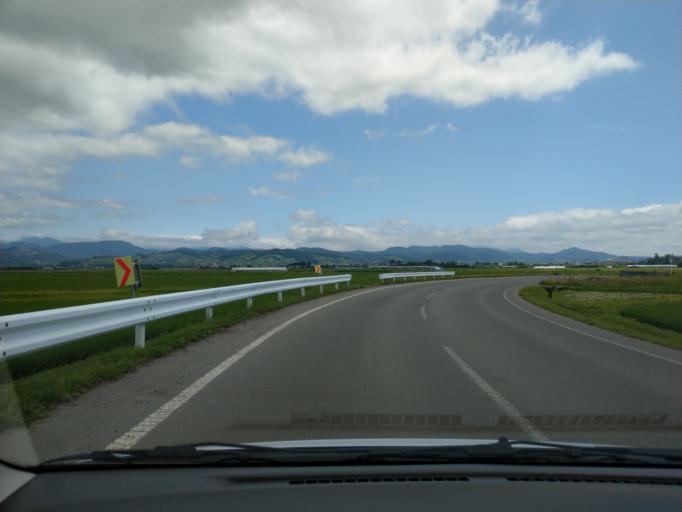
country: JP
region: Aomori
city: Kuroishi
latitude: 40.6300
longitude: 140.5639
